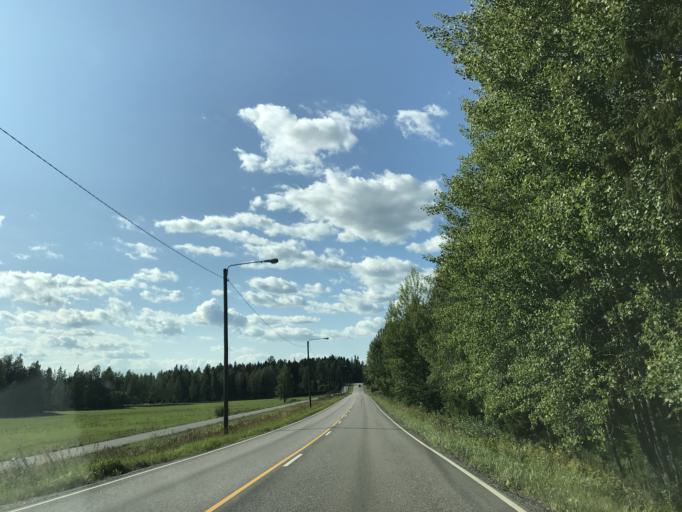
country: FI
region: Uusimaa
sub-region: Helsinki
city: Nurmijaervi
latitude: 60.4104
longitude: 24.8861
